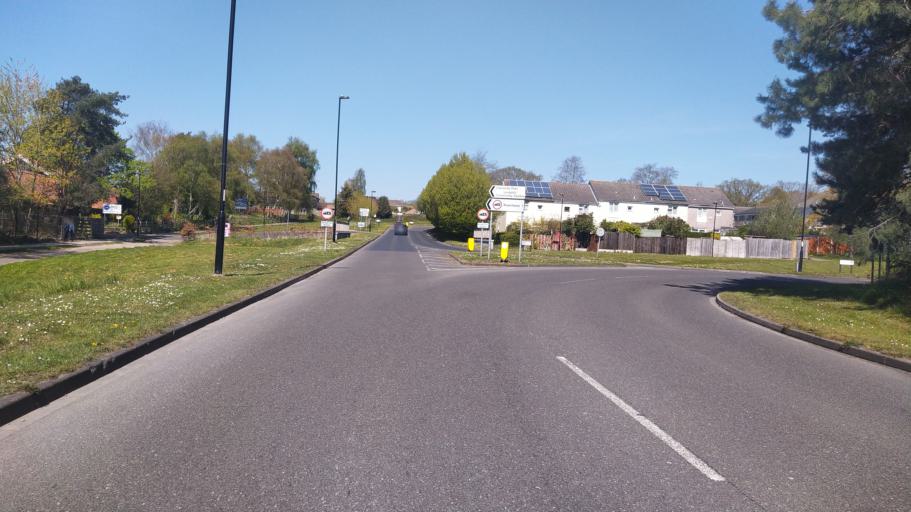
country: GB
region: England
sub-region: Hampshire
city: Totton
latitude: 50.9423
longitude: -1.4505
